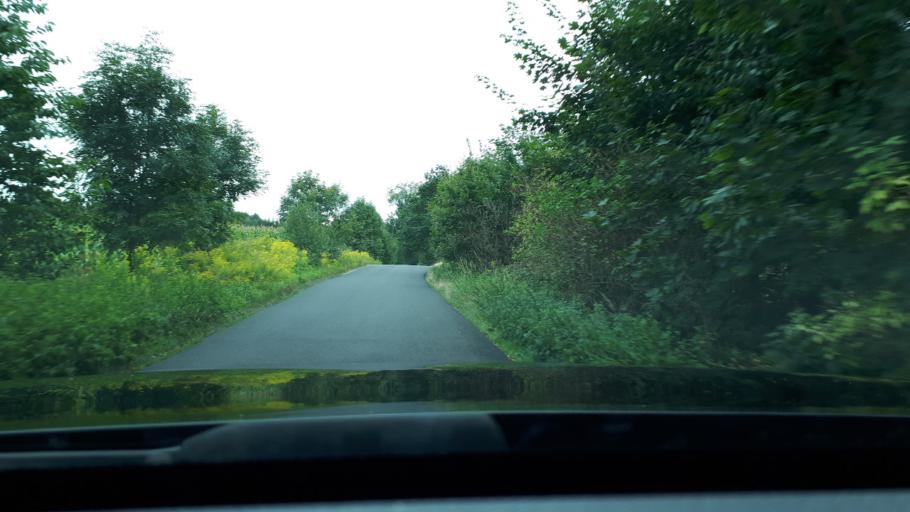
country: PL
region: Lower Silesian Voivodeship
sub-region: Powiat lubanski
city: Olszyna
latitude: 51.0357
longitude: 15.3323
